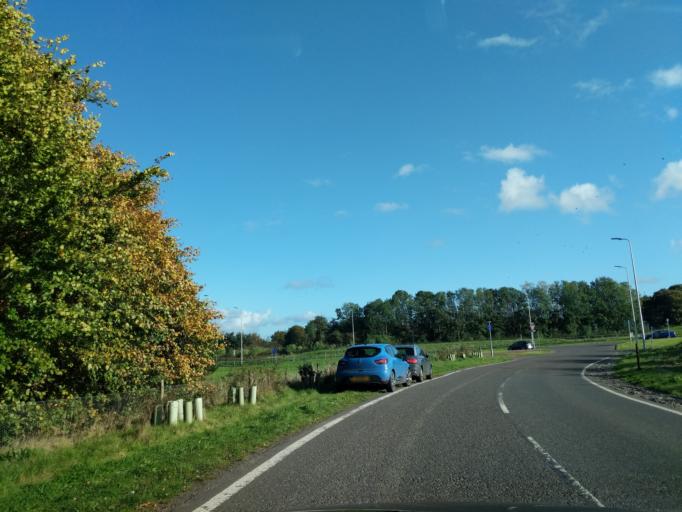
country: GB
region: Scotland
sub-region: Dumfries and Galloway
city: Dumfries
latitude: 55.0610
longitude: -3.6572
